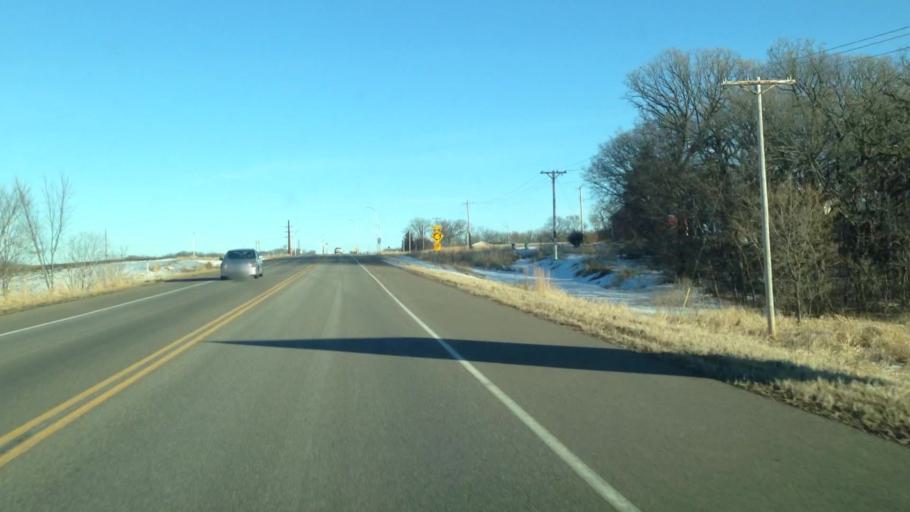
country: US
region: Minnesota
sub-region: Rice County
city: Lonsdale
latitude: 44.5438
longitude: -93.4471
